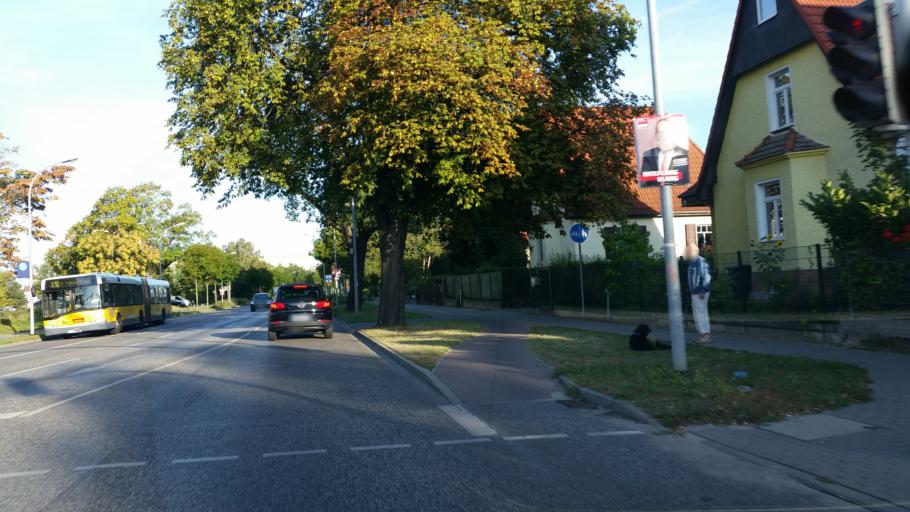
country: DE
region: Brandenburg
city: Teltow
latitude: 52.3976
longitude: 13.2753
